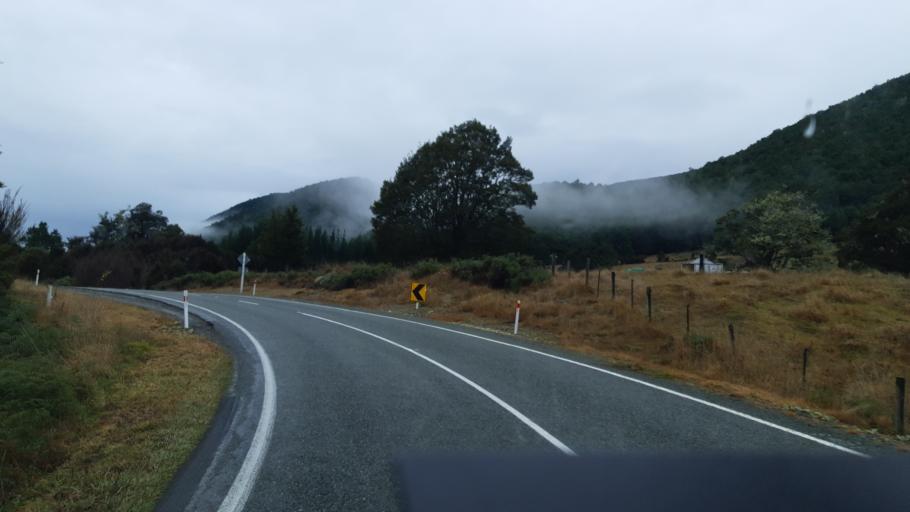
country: NZ
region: Tasman
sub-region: Tasman District
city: Wakefield
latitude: -41.7585
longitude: 172.9000
